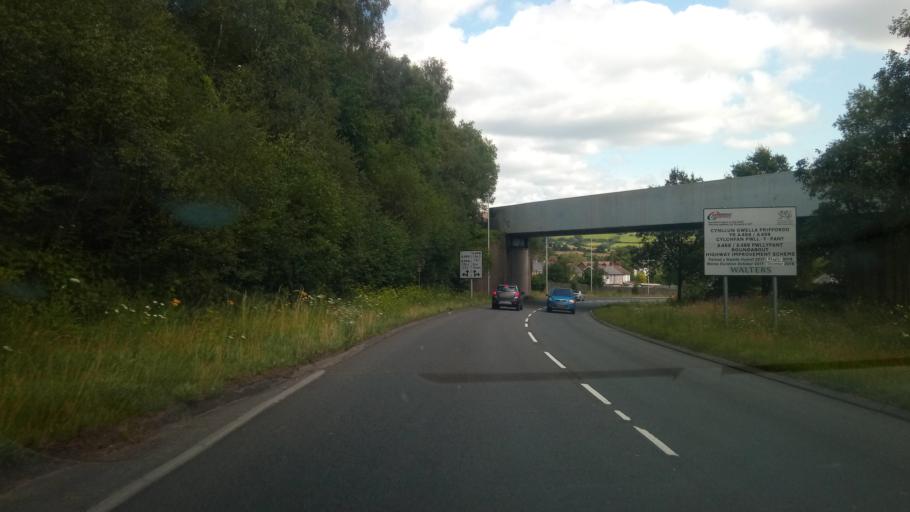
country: GB
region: Wales
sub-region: Caerphilly County Borough
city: Llanbradach
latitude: 51.5907
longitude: -3.2303
